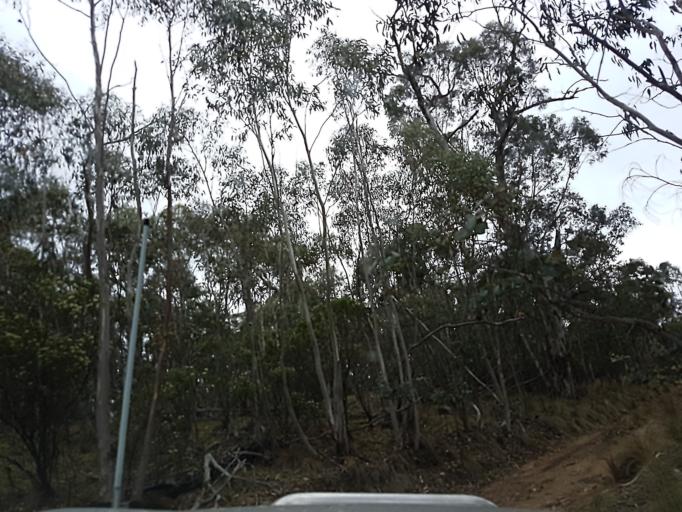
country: AU
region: New South Wales
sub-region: Snowy River
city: Jindabyne
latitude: -36.8859
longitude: 148.3379
